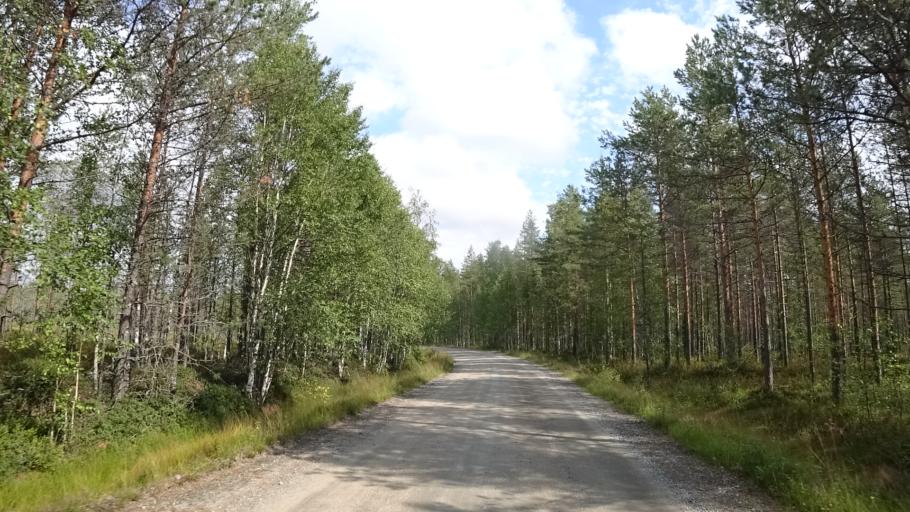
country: FI
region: North Karelia
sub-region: Joensuu
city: Ilomantsi
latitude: 62.9327
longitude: 31.4247
